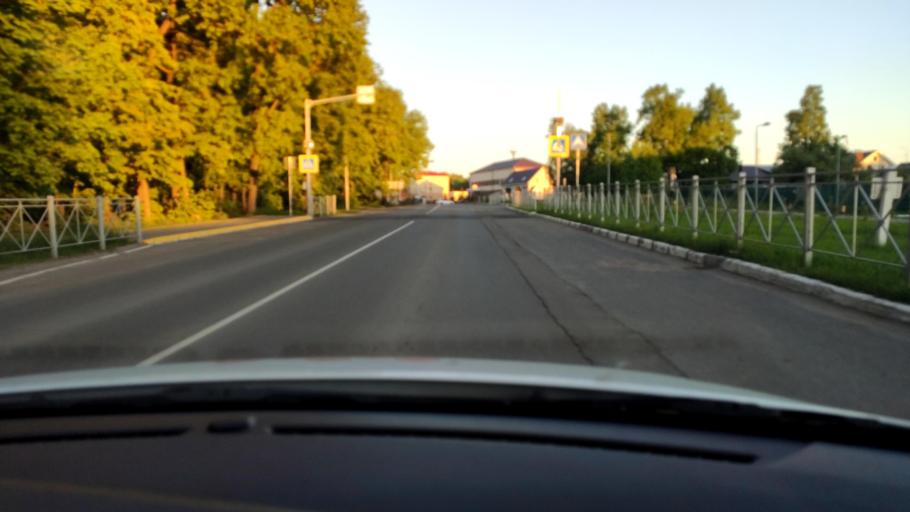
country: RU
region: Tatarstan
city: Vysokaya Gora
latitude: 55.9233
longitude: 49.3053
